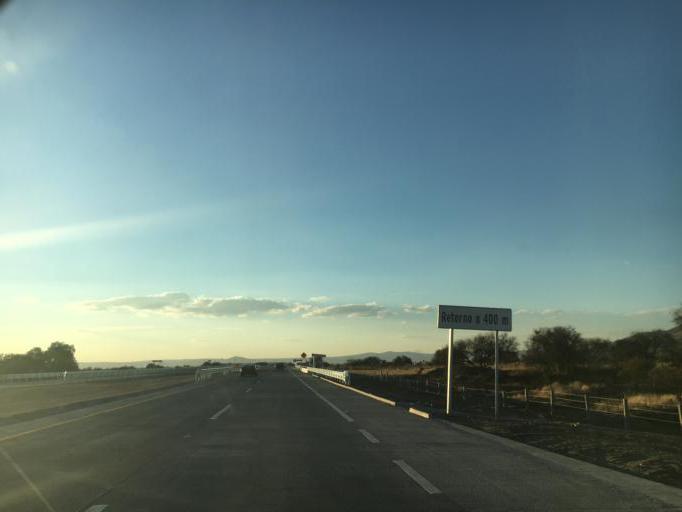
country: MX
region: Guanajuato
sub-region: Leon
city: Ladrilleras del Refugio
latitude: 21.0968
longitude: -101.5678
